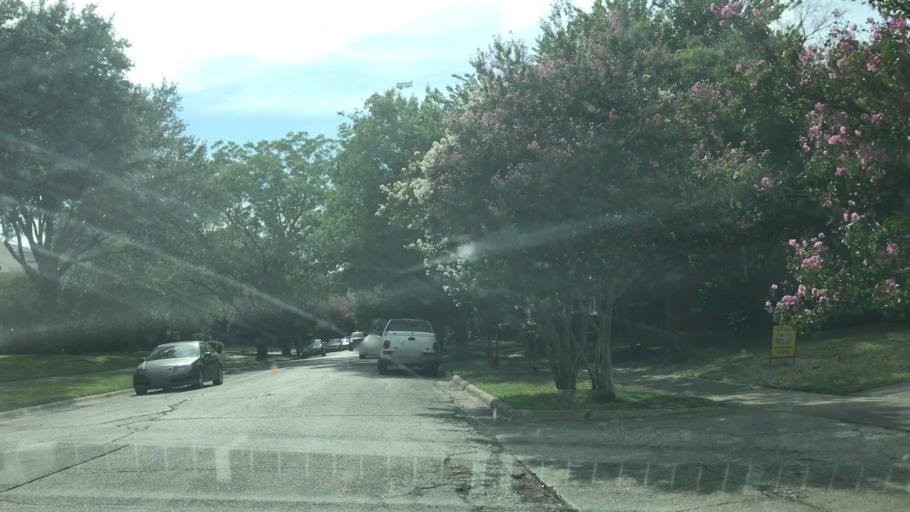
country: US
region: Texas
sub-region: Dallas County
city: Highland Park
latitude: 32.8069
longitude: -96.7653
